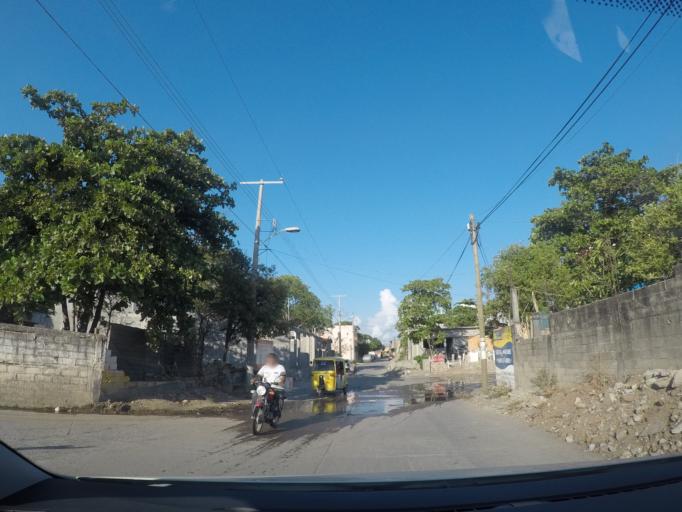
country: MX
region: Oaxaca
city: Juchitan de Zaragoza
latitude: 16.4394
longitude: -95.0290
